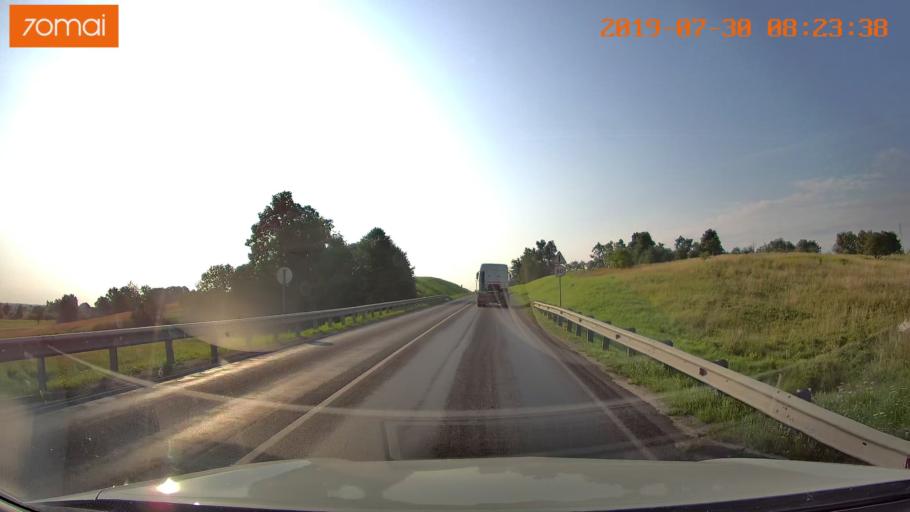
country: RU
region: Kaliningrad
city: Chernyakhovsk
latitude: 54.6246
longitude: 21.5428
